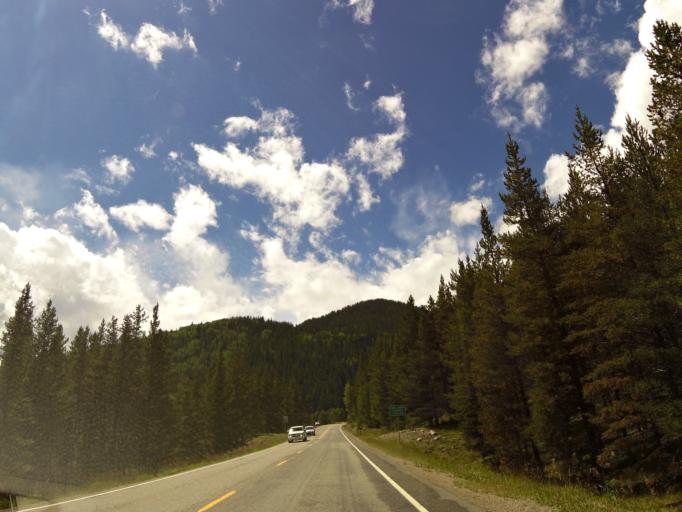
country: US
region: Colorado
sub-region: San Juan County
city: Silverton
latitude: 37.7204
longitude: -107.7519
